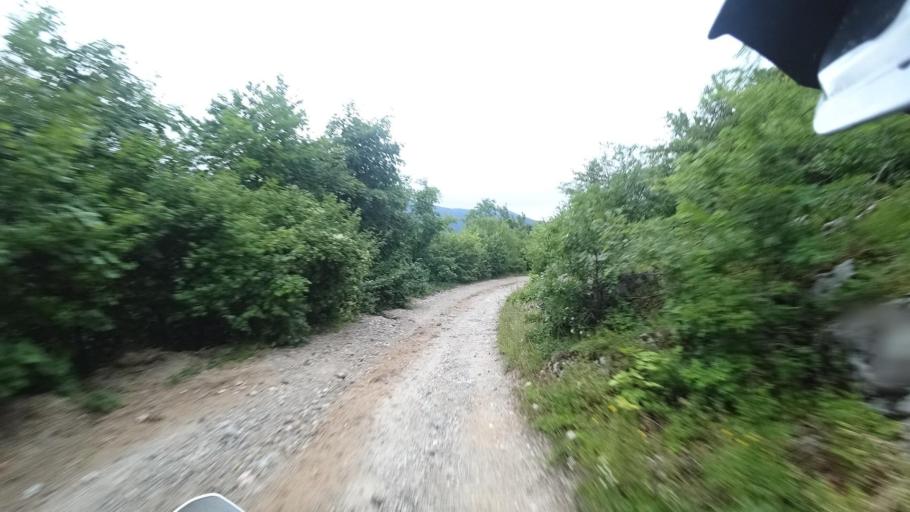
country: BA
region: Federation of Bosnia and Herzegovina
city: Orasac
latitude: 44.4923
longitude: 15.9695
